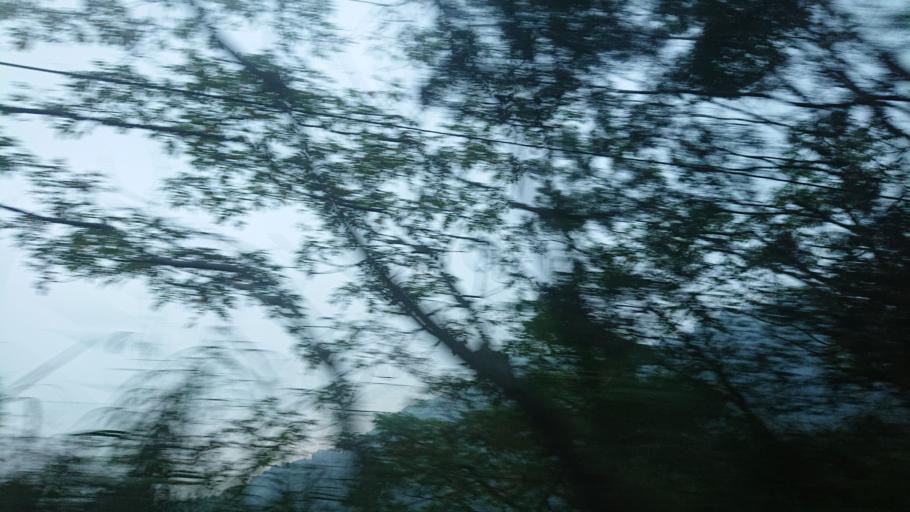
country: TW
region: Taiwan
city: Lugu
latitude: 23.5961
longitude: 120.7223
